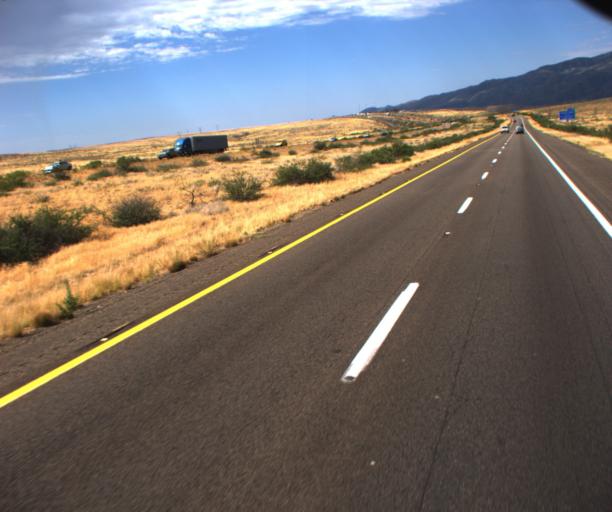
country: US
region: Arizona
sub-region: Yavapai County
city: Cordes Lakes
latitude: 34.2040
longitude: -112.1235
